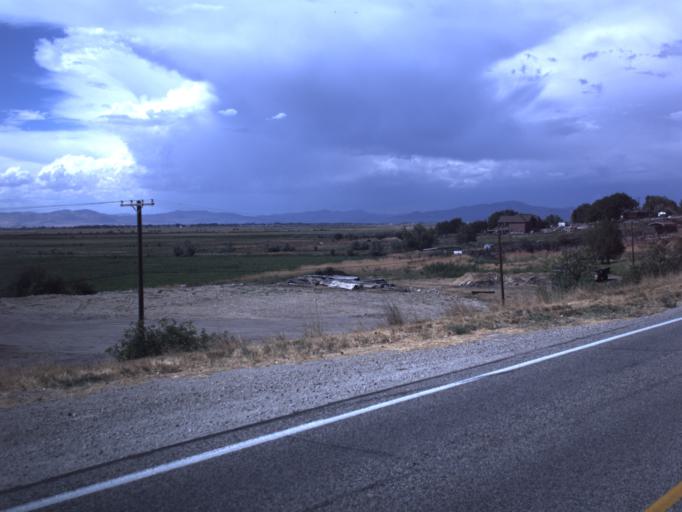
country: US
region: Utah
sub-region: Box Elder County
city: Brigham City
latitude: 41.5546
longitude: -112.0201
